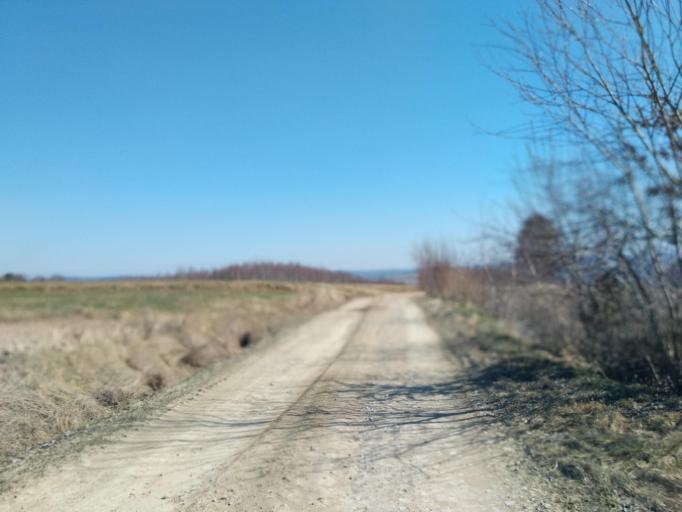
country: PL
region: Subcarpathian Voivodeship
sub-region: Powiat ropczycko-sedziszowski
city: Niedzwiada
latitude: 49.9547
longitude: 21.5551
